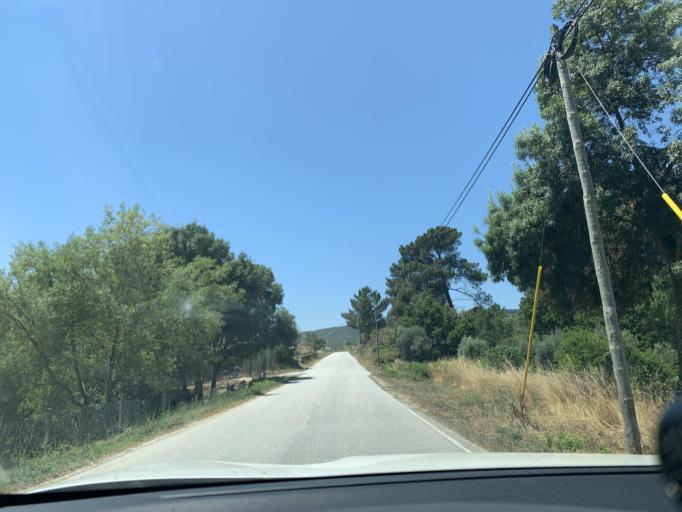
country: PT
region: Guarda
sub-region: Fornos de Algodres
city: Fornos de Algodres
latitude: 40.5809
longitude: -7.6178
